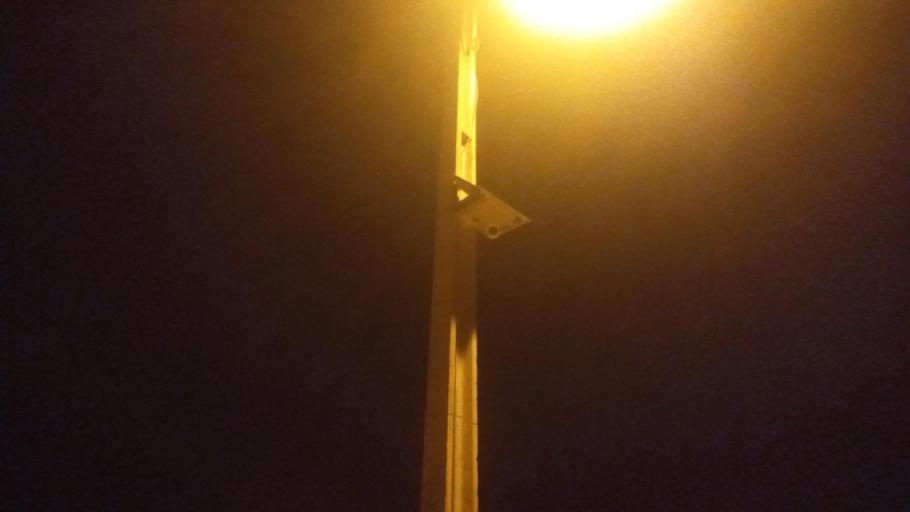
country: TN
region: Tataouine
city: Remada
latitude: 32.3105
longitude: 10.4070
